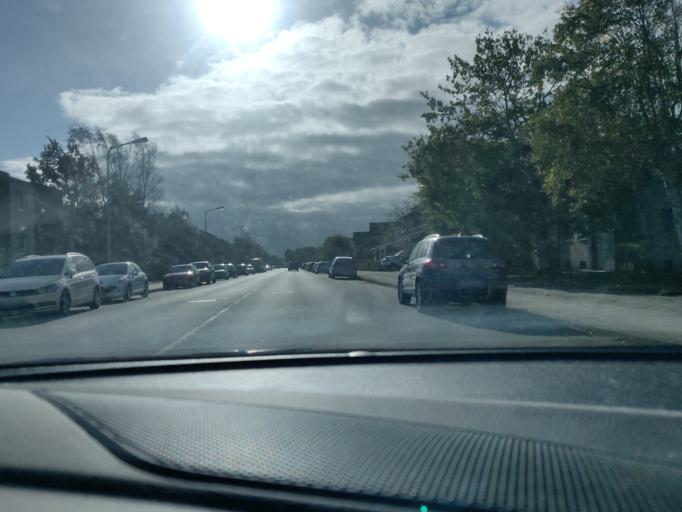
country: DE
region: Lower Saxony
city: Cuxhaven
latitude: 53.8710
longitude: 8.6784
